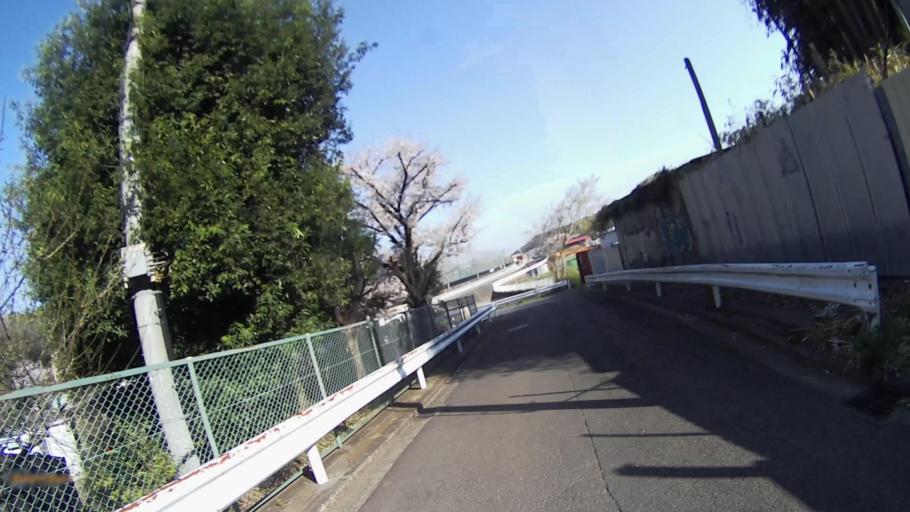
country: JP
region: Kanagawa
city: Atsugi
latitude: 35.4359
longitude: 139.4138
